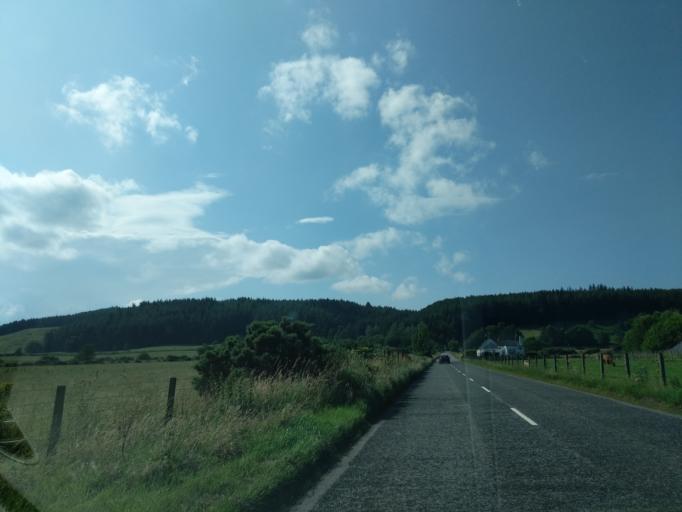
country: GB
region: Scotland
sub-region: Moray
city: Rothes
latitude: 57.5521
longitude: -3.1465
